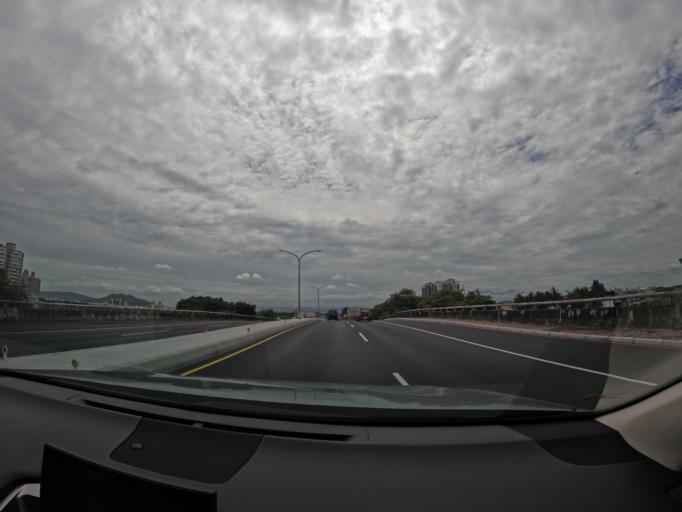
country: TW
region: Kaohsiung
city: Kaohsiung
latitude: 22.7847
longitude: 120.3011
